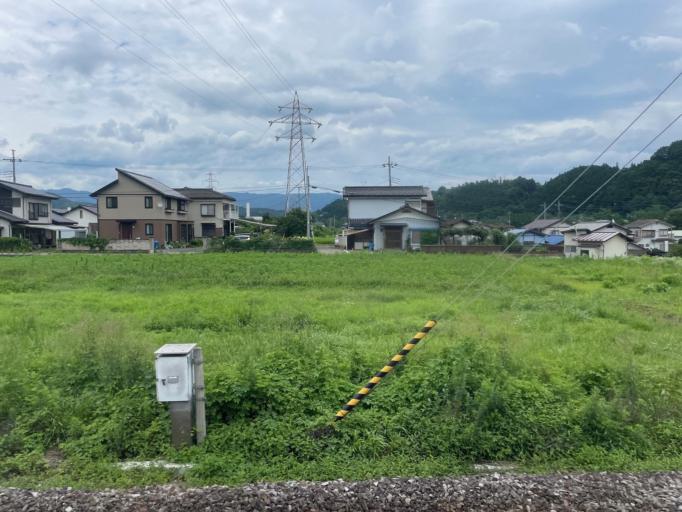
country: JP
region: Gunma
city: Numata
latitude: 36.6501
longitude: 139.0305
